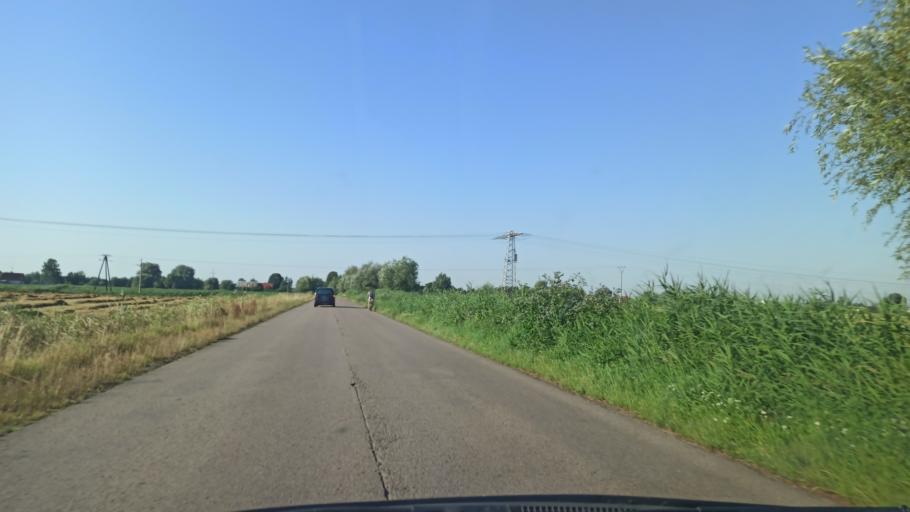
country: PL
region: Warmian-Masurian Voivodeship
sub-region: Powiat elblaski
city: Elblag
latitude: 54.1791
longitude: 19.3320
